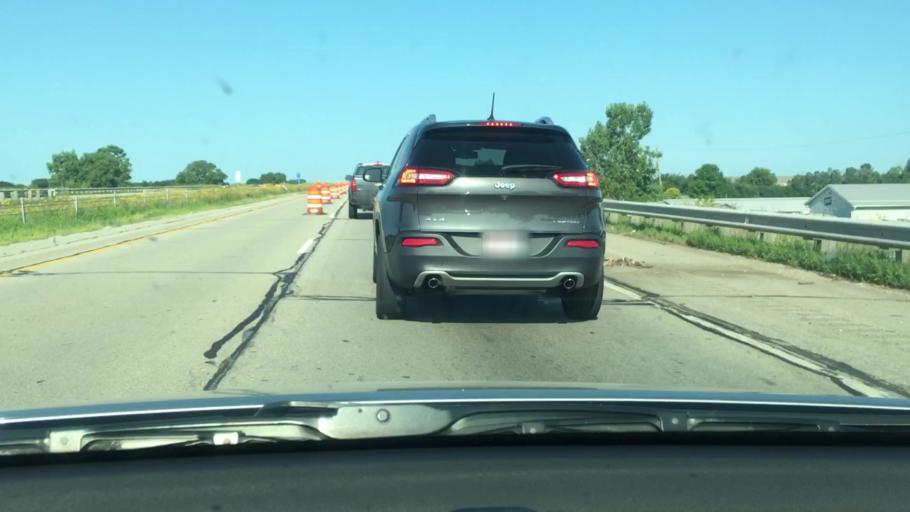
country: US
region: Wisconsin
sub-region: Outagamie County
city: Appleton
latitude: 44.2990
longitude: -88.4314
